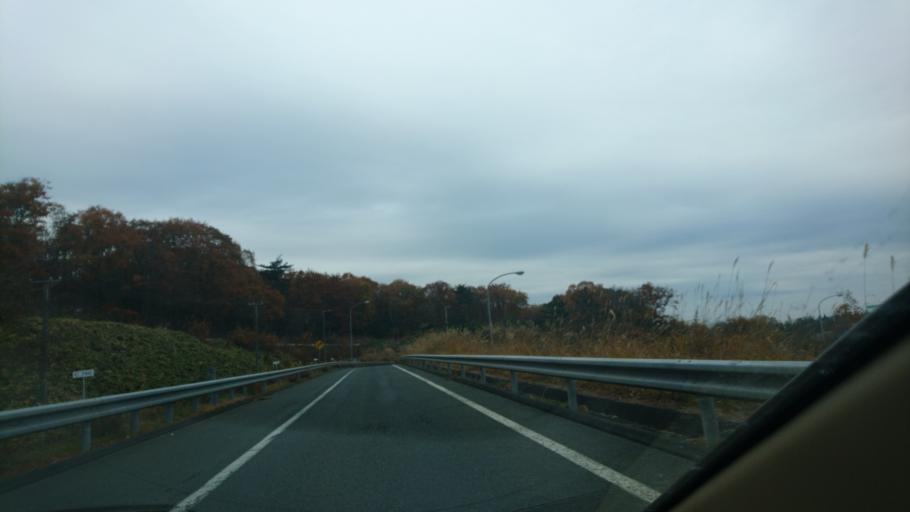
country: JP
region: Iwate
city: Kitakami
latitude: 39.2409
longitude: 141.0779
